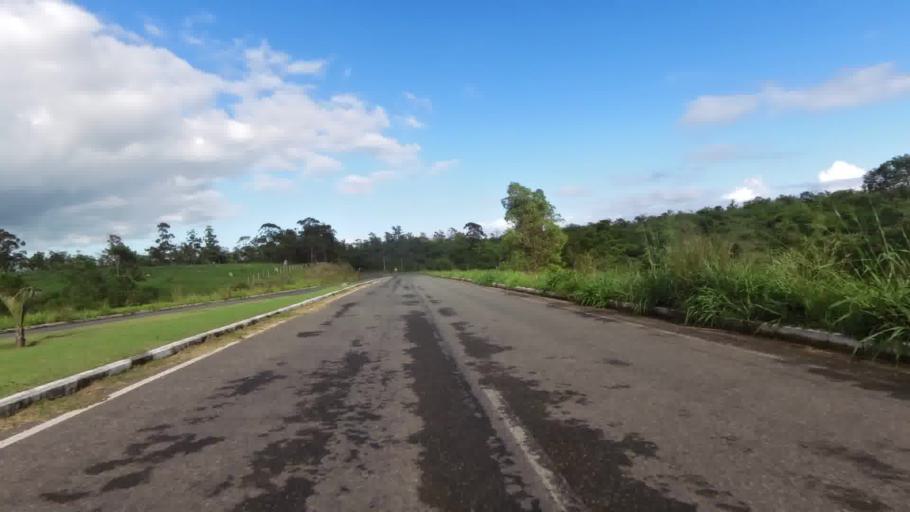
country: BR
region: Espirito Santo
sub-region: Piuma
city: Piuma
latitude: -20.7969
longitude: -40.6228
